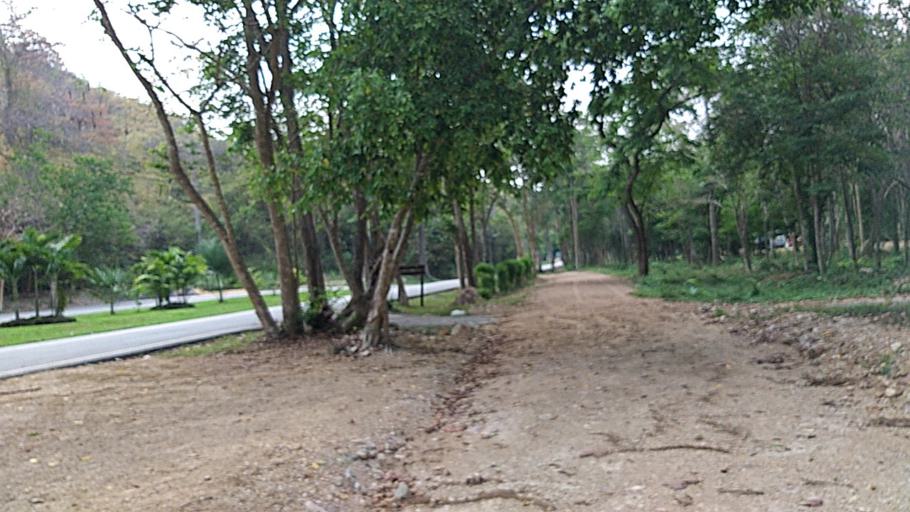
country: TH
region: Sara Buri
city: Wihan Daeng
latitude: 14.4384
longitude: 100.9619
